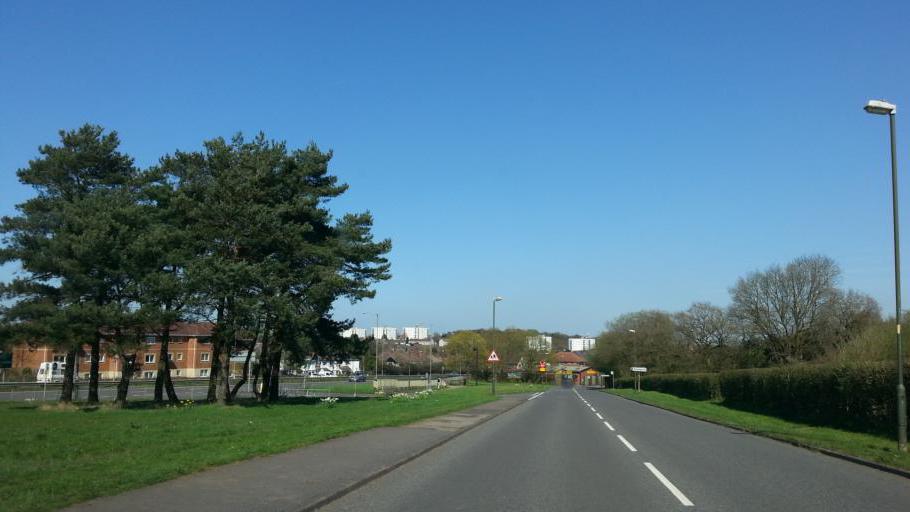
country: GB
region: England
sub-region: Worcestershire
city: Barnt Green
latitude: 52.3900
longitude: -2.0278
